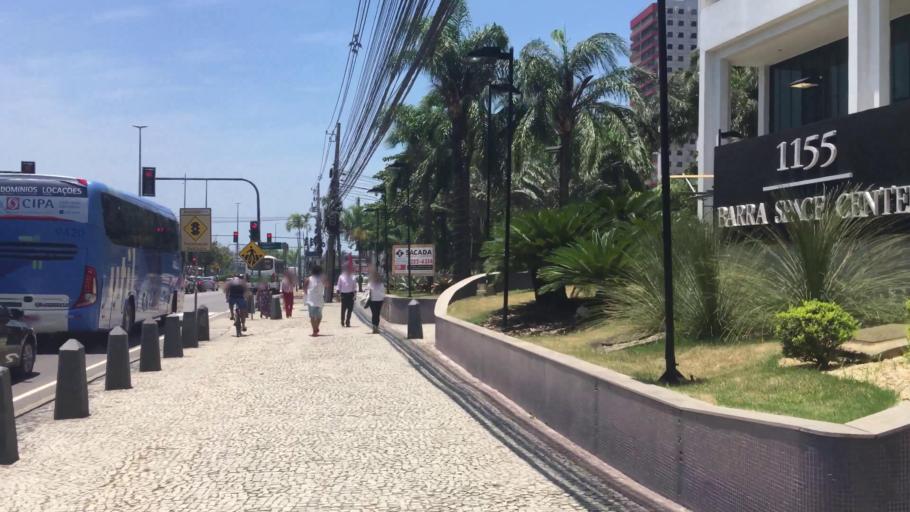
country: BR
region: Rio de Janeiro
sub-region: Rio De Janeiro
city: Rio de Janeiro
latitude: -23.0031
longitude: -43.3257
